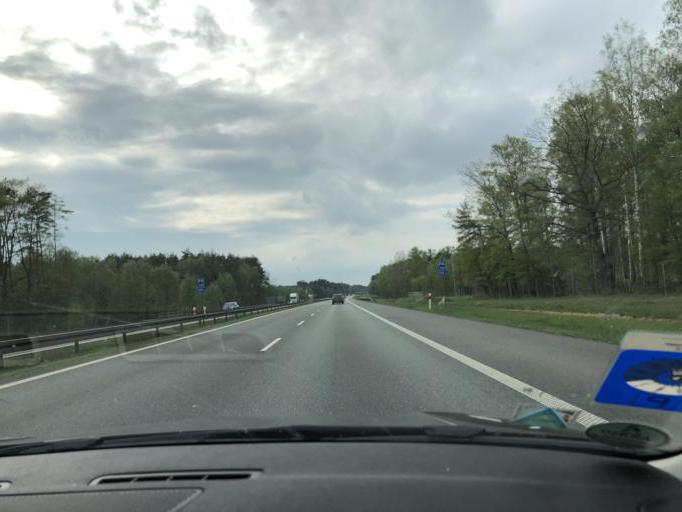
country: PL
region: Opole Voivodeship
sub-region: Powiat opolski
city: Dabrowa
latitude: 50.6656
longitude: 17.6836
